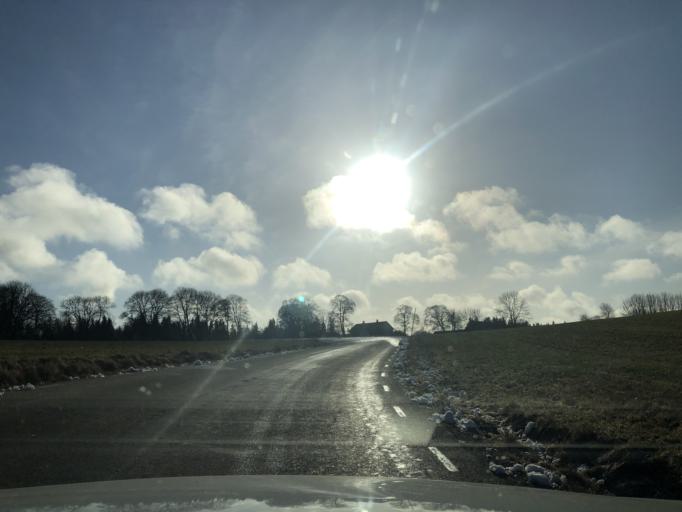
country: SE
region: Vaestra Goetaland
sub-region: Ulricehamns Kommun
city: Ulricehamn
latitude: 57.8048
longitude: 13.5480
